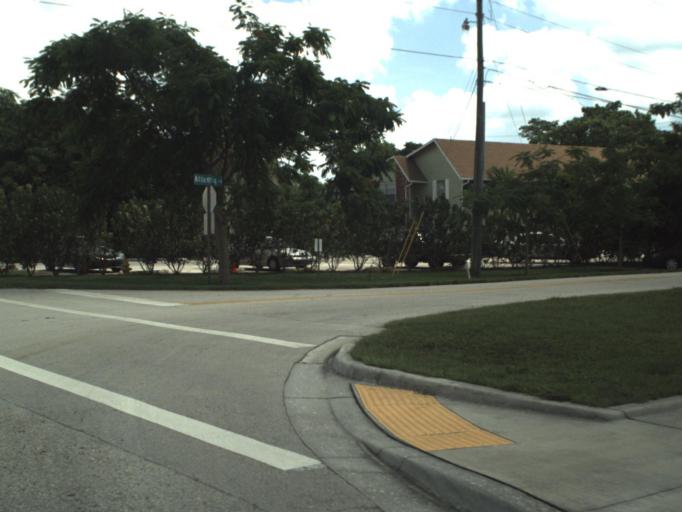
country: US
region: Florida
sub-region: Palm Beach County
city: North Palm Beach
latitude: 26.8533
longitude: -80.0961
